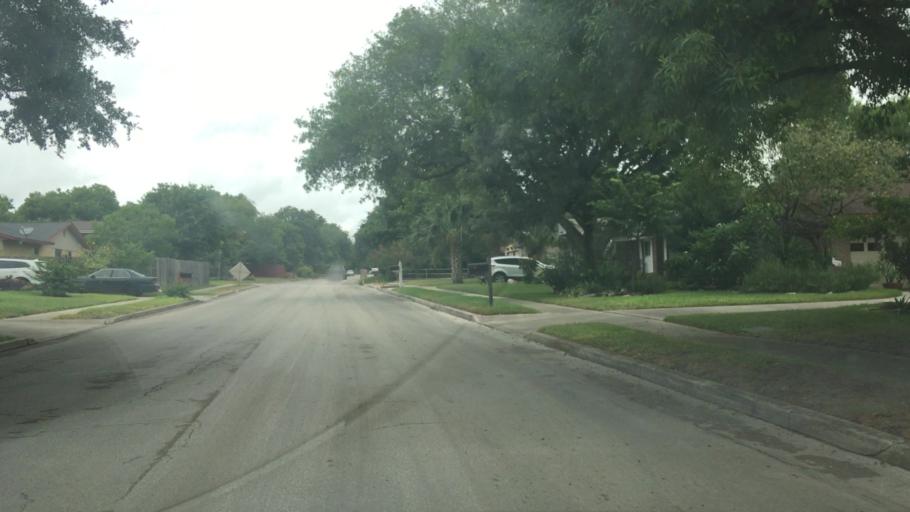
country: US
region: Texas
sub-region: Bexar County
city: Universal City
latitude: 29.5487
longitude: -98.3154
